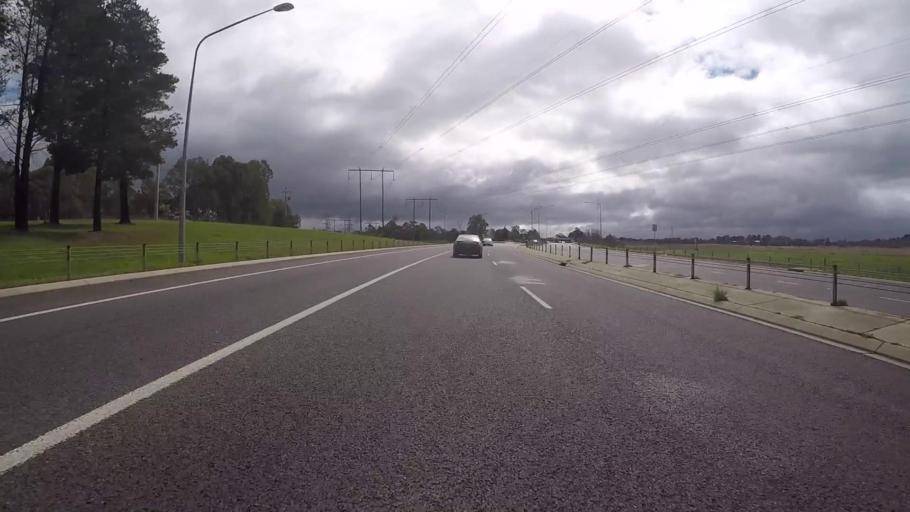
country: AU
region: Australian Capital Territory
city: Kaleen
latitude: -35.2320
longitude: 149.1251
